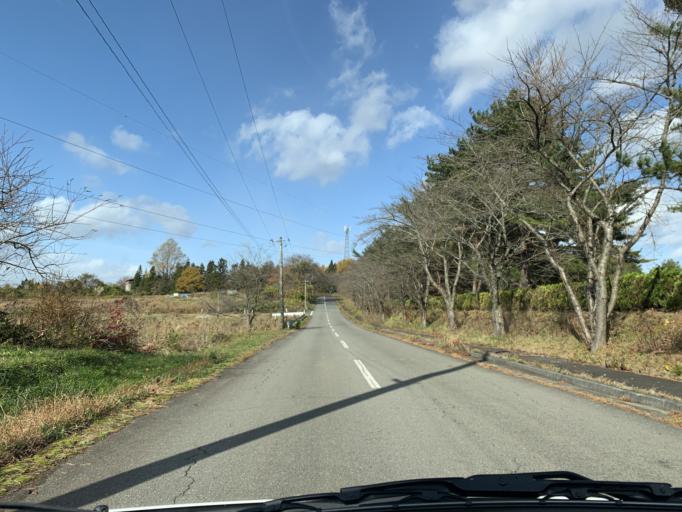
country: JP
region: Iwate
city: Mizusawa
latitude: 39.0362
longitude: 141.0843
